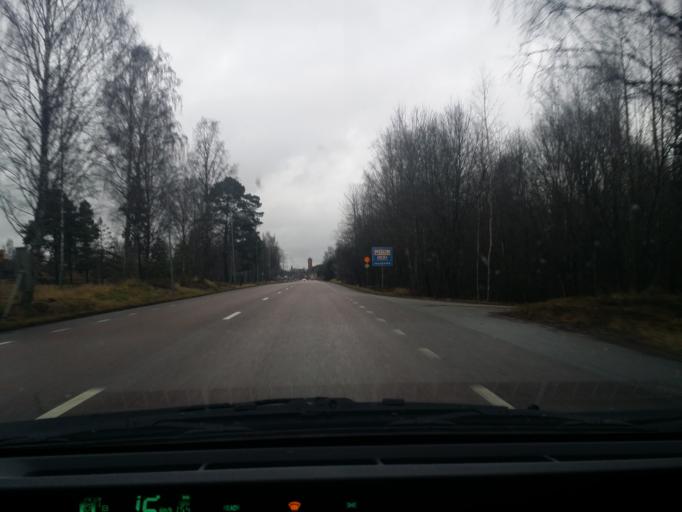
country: SE
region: Vaestmanland
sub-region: Sala Kommun
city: Sala
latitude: 59.9036
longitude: 16.5791
